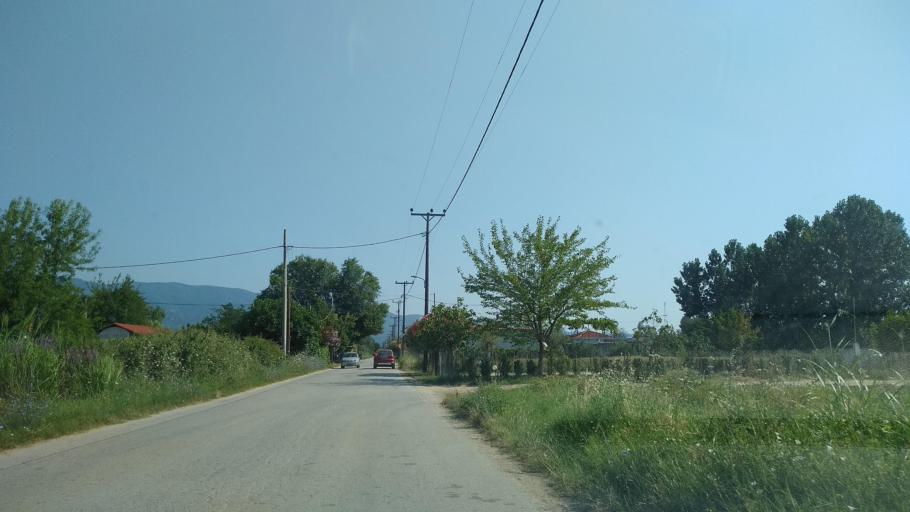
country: GR
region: Central Macedonia
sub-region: Nomos Thessalonikis
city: Stavros
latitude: 40.6834
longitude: 23.6878
